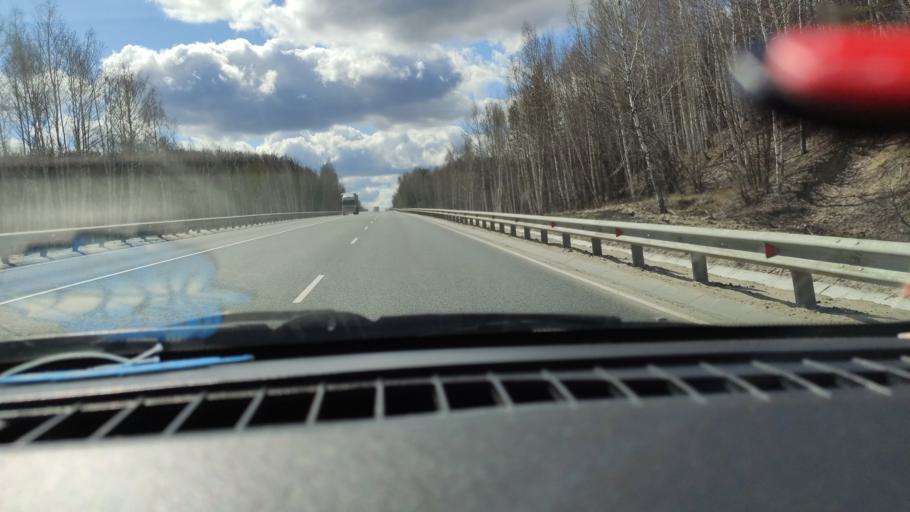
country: RU
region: Saratov
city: Khvalynsk
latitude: 52.4965
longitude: 48.0145
